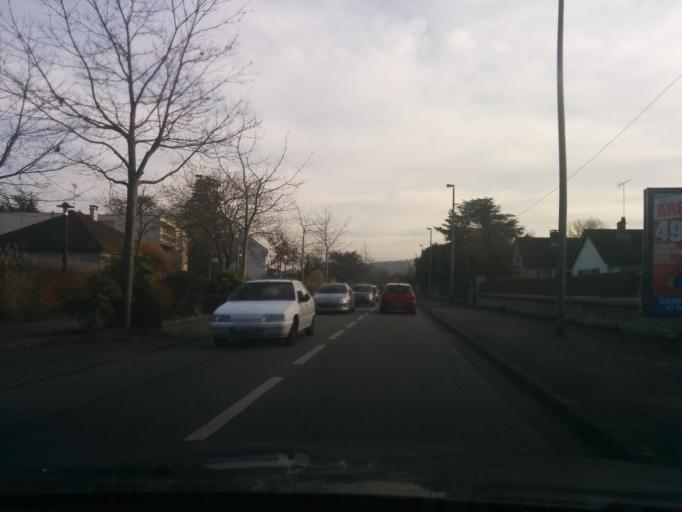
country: FR
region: Haute-Normandie
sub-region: Departement de l'Eure
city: Vernon
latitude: 49.0880
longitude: 1.4727
